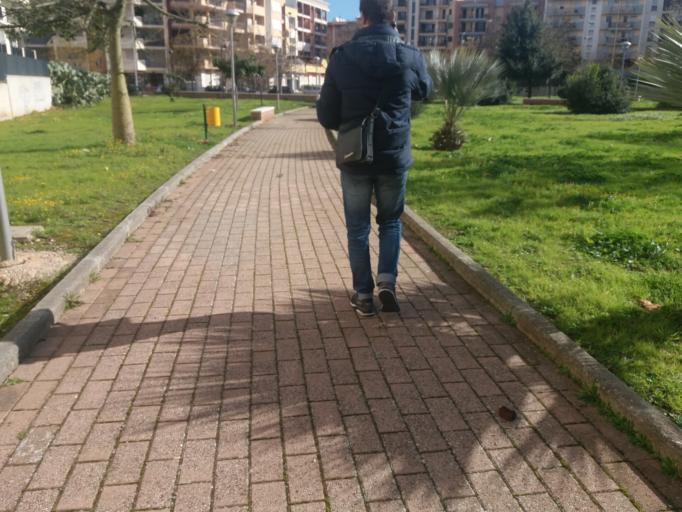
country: IT
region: Apulia
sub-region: Provincia di Barletta - Andria - Trani
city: Andria
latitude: 41.2356
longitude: 16.3002
